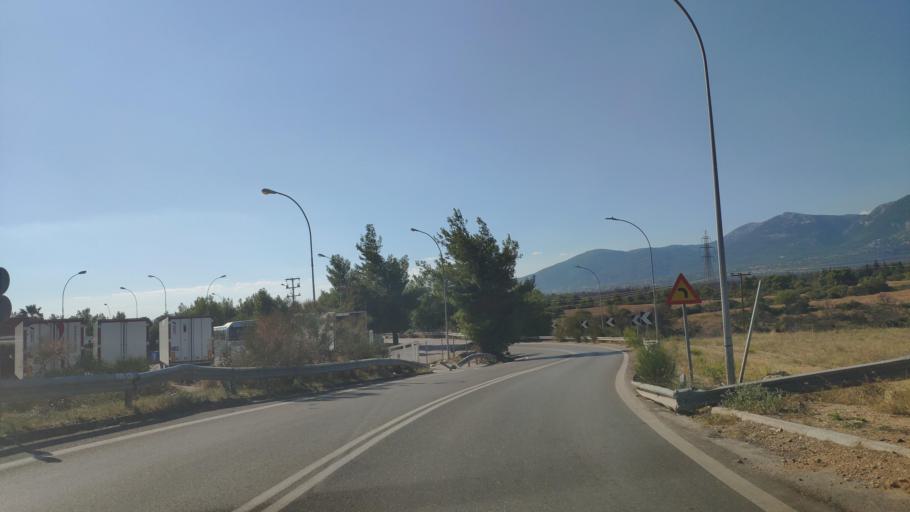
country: GR
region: Attica
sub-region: Nomarchia Athinas
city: Ekali
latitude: 38.1141
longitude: 23.8251
